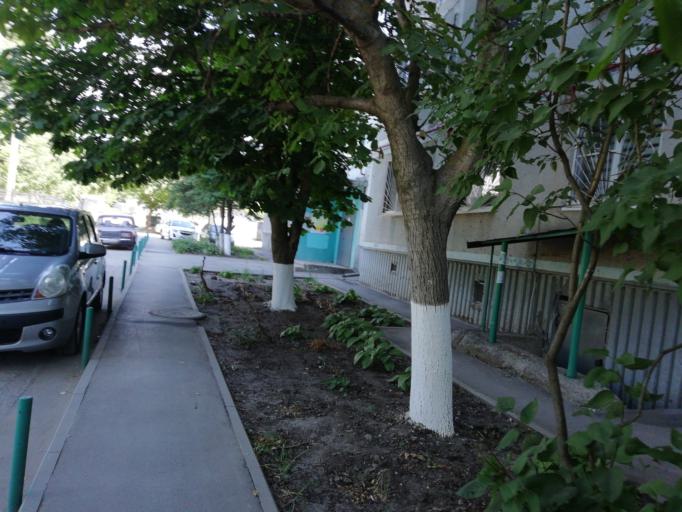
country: RU
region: Rostov
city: Severnyy
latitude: 47.2858
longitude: 39.7123
